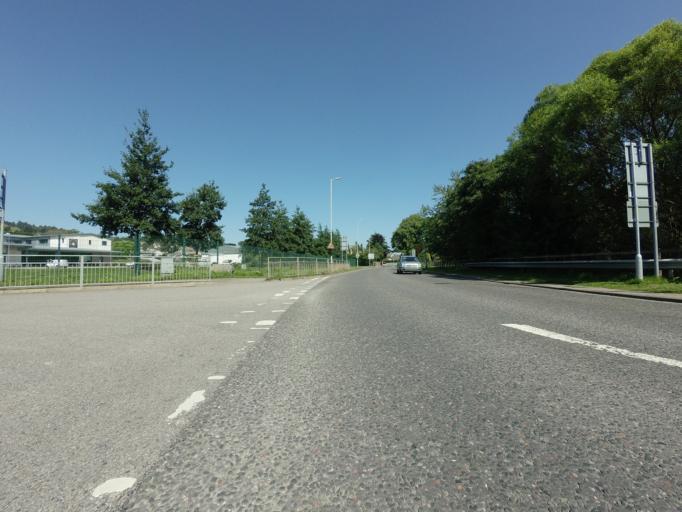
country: GB
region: Scotland
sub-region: Highland
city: Dingwall
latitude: 57.6000
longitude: -4.4318
